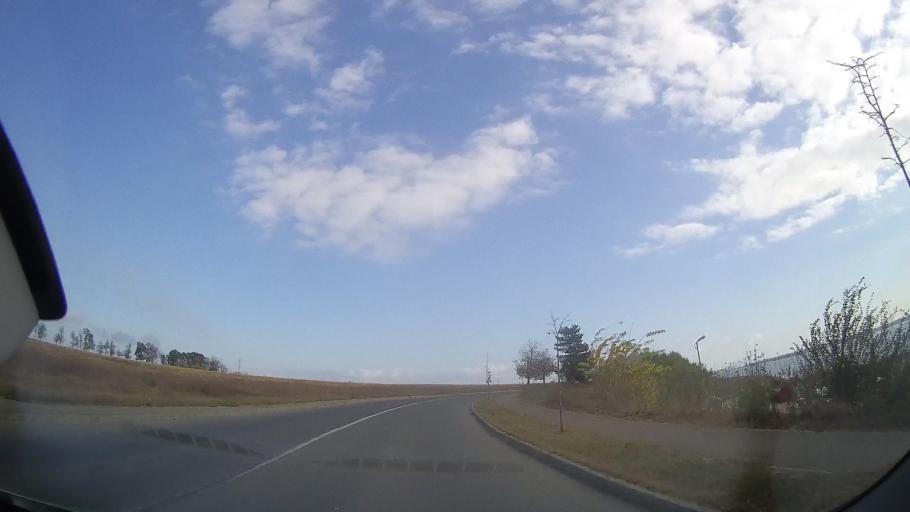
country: RO
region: Constanta
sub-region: Oras Techirghiol
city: Techirghiol
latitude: 44.0576
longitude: 28.6097
